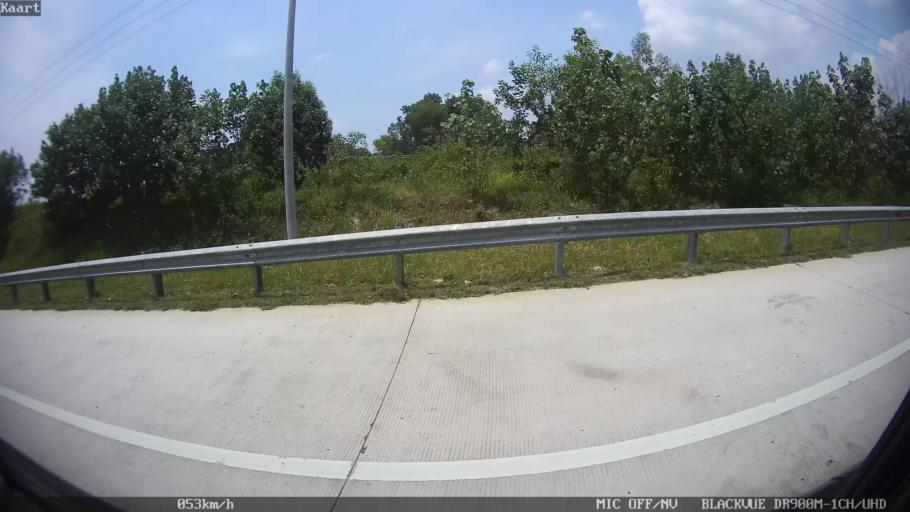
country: ID
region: Lampung
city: Natar
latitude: -5.2821
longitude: 105.2041
